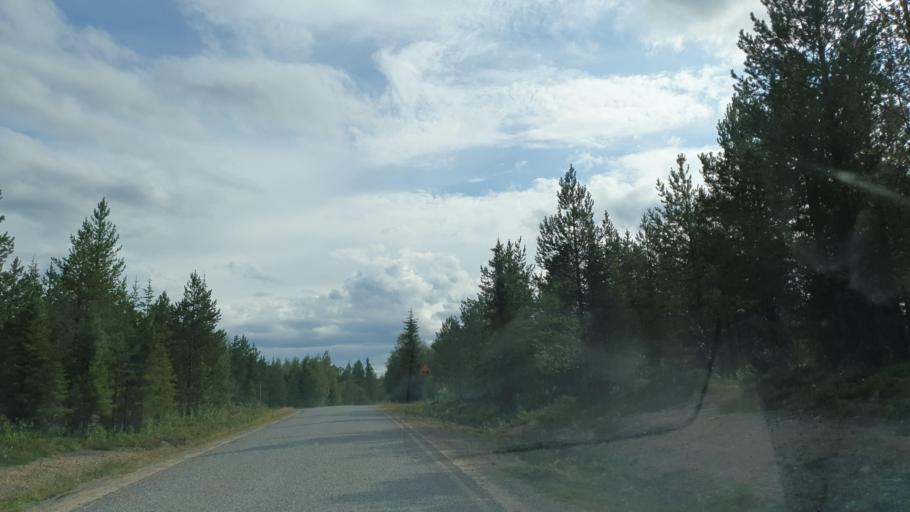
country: FI
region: Lapland
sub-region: Tunturi-Lappi
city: Muonio
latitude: 67.6878
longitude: 24.1101
